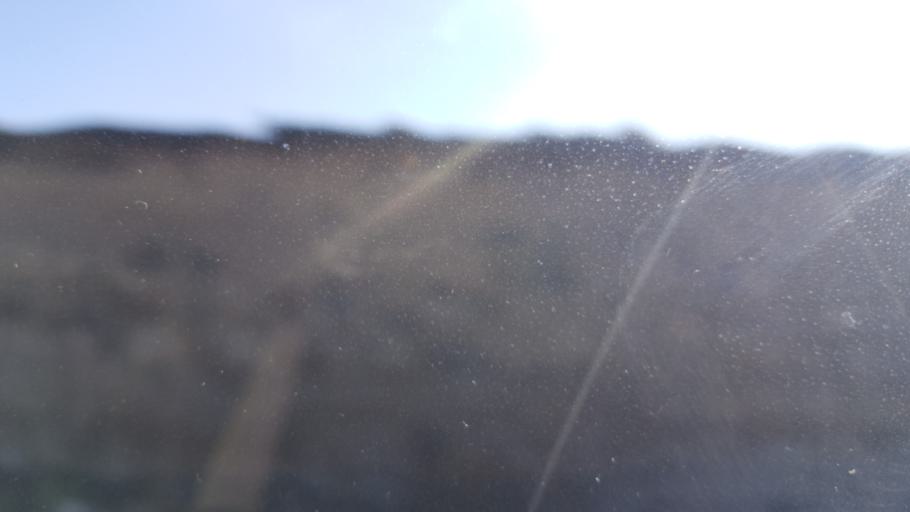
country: TR
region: Ankara
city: Yenice
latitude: 39.2744
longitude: 32.6760
